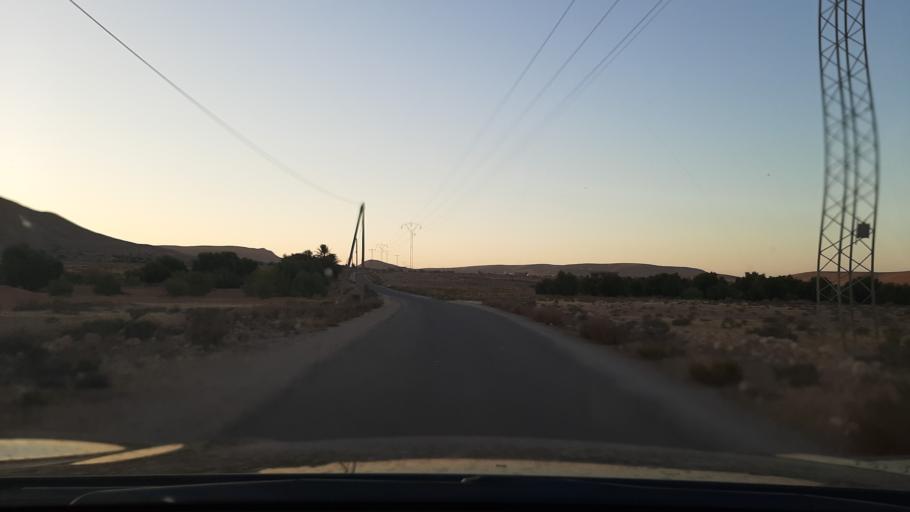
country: TN
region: Qabis
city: Matmata
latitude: 33.5474
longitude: 10.1909
